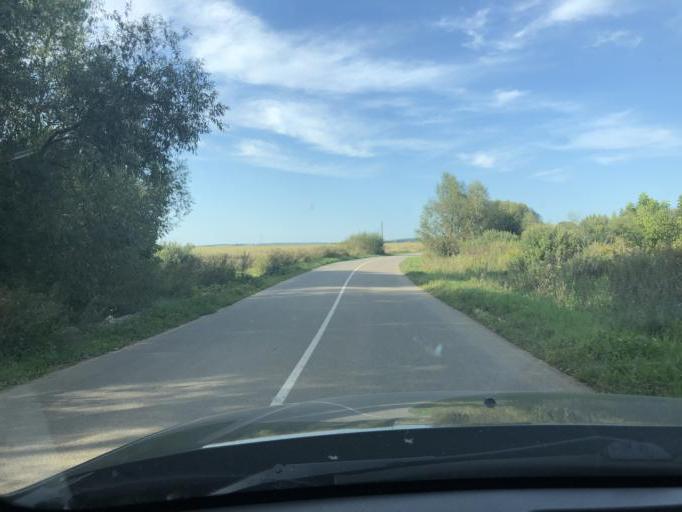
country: RU
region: Tula
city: Krapivna
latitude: 54.1207
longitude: 37.1533
